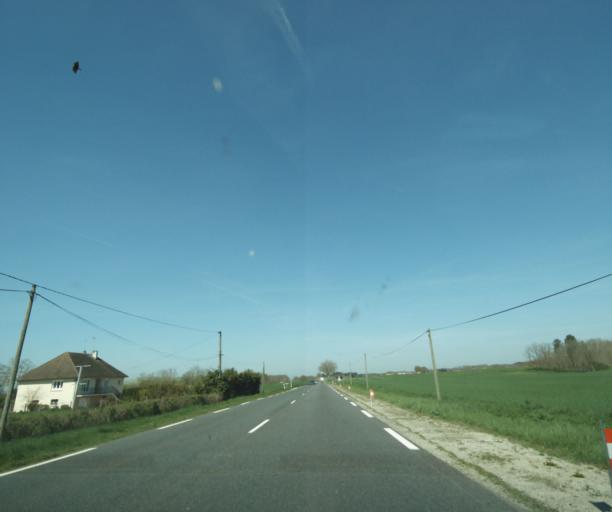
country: FR
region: Auvergne
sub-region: Departement de l'Allier
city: Trevol
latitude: 46.6687
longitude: 3.2393
